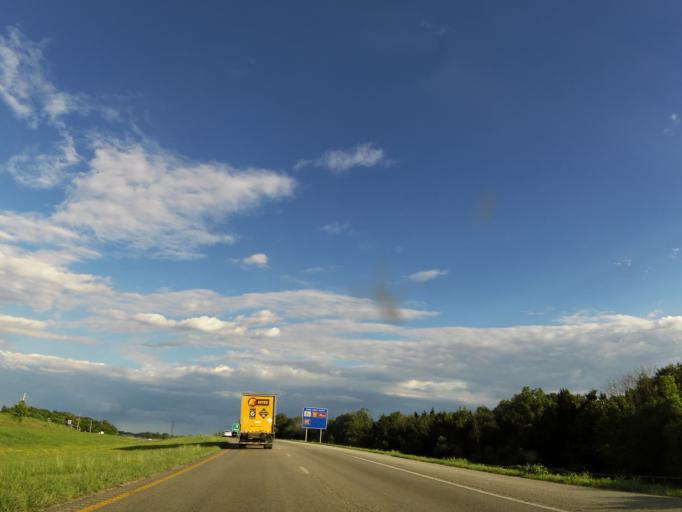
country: US
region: Missouri
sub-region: Saint Charles County
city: Wentzville
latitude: 38.8304
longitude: -90.8549
